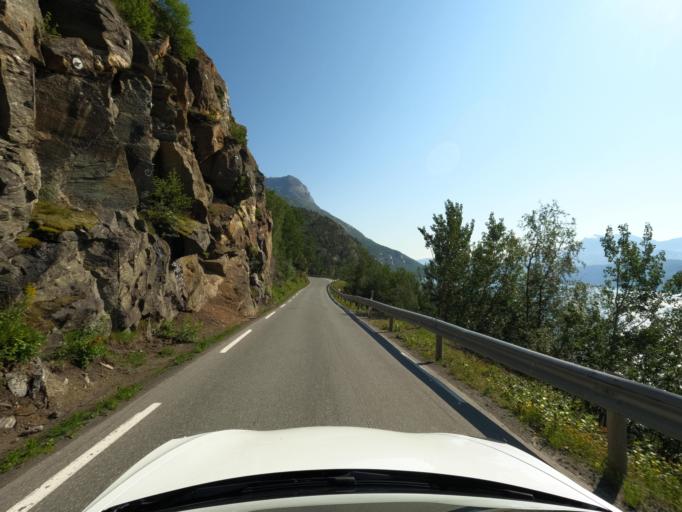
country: NO
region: Nordland
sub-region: Narvik
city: Narvik
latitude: 68.3669
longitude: 17.2556
